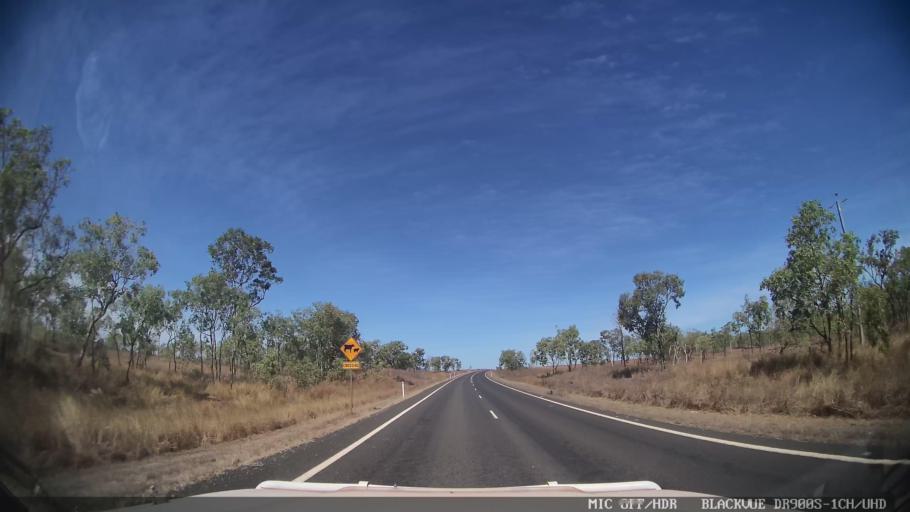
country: AU
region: Queensland
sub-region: Cook
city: Cooktown
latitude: -15.7907
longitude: 144.7070
